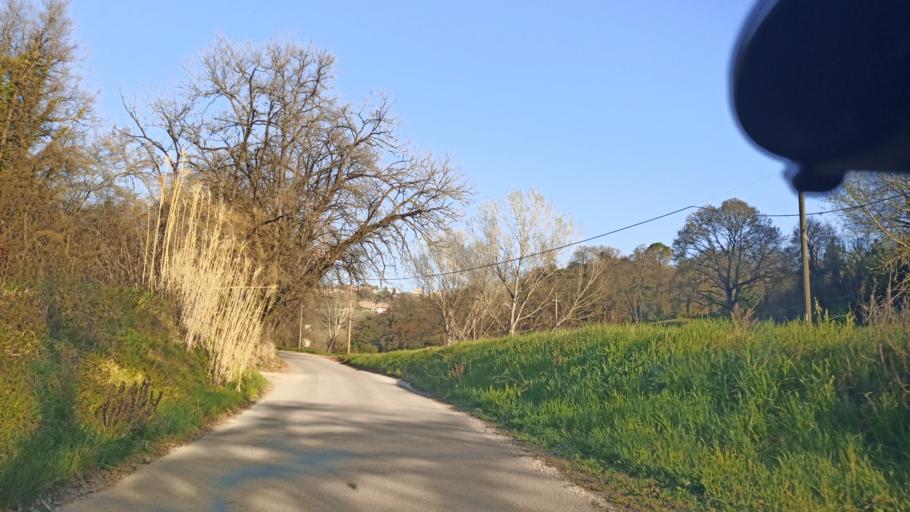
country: IT
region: Latium
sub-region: Provincia di Rieti
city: Poggio Mirteto
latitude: 42.2625
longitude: 12.6708
